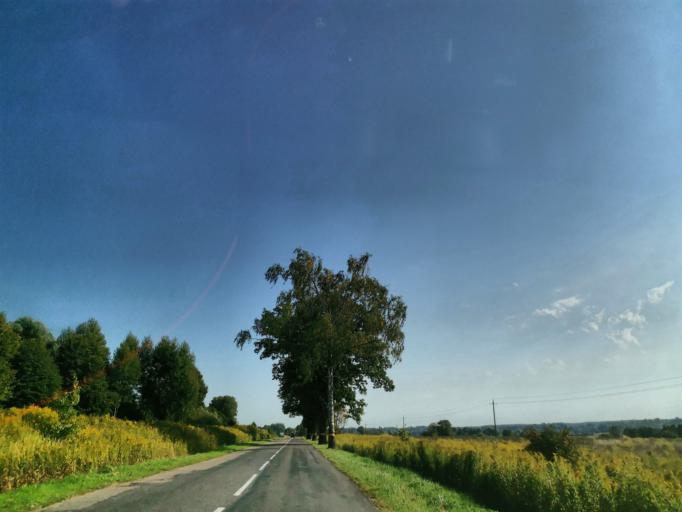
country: RU
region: Kaliningrad
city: Chernyakhovsk
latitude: 54.7036
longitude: 21.8824
